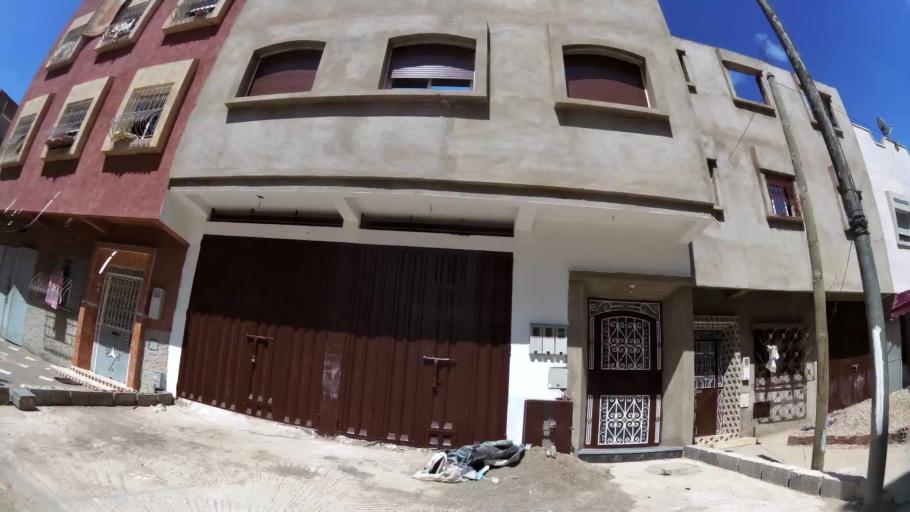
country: MA
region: Gharb-Chrarda-Beni Hssen
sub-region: Kenitra Province
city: Kenitra
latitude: 34.2288
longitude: -6.5502
